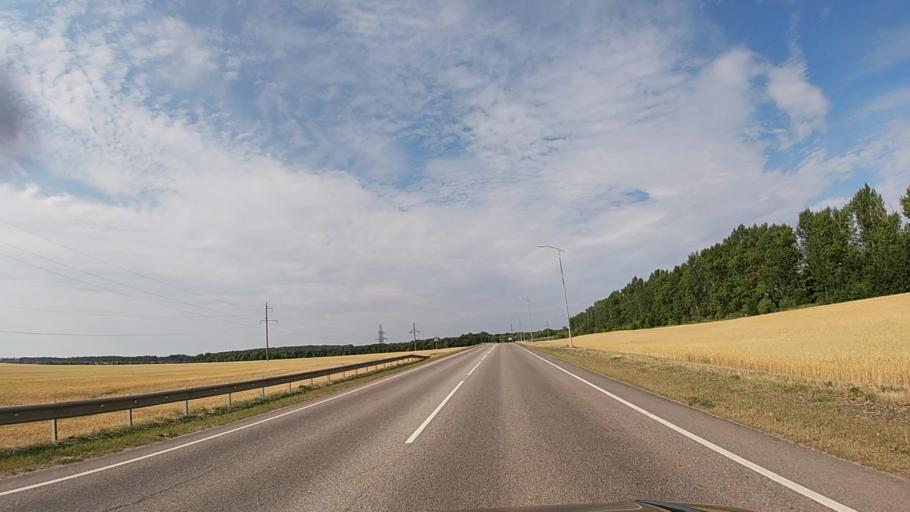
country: RU
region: Belgorod
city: Proletarskiy
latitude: 50.8079
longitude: 35.7444
